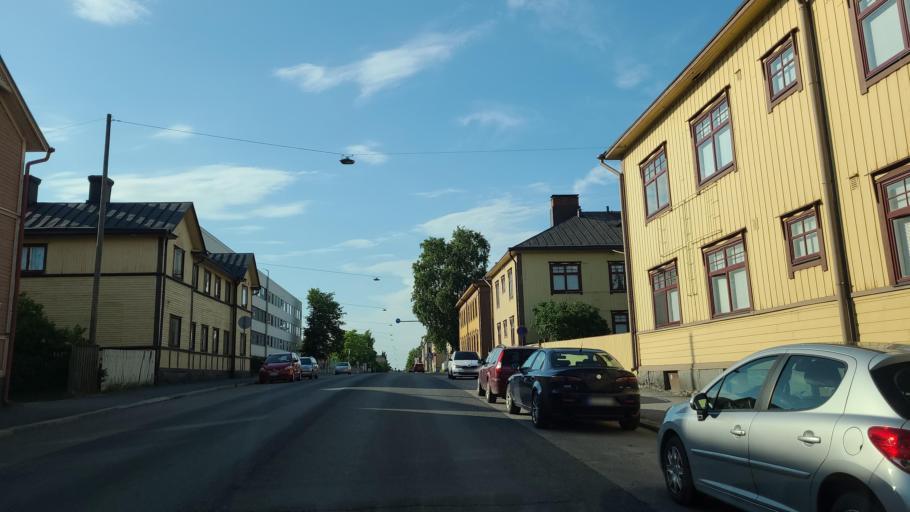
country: FI
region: Ostrobothnia
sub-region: Vaasa
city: Vaasa
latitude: 63.0998
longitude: 21.6221
